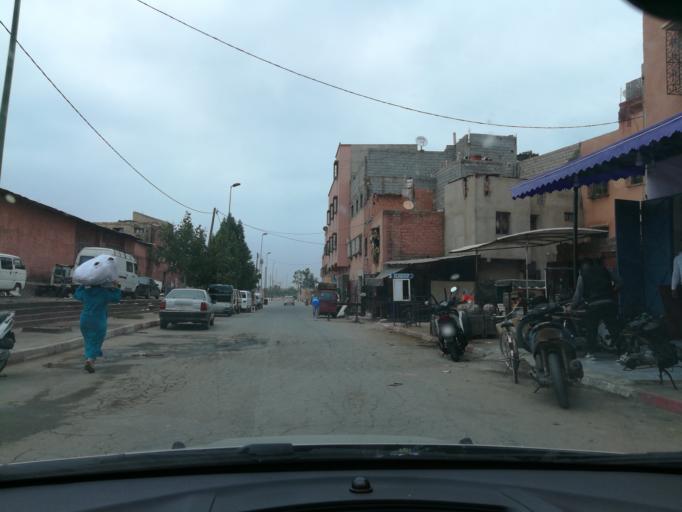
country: MA
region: Marrakech-Tensift-Al Haouz
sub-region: Marrakech
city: Marrakesh
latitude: 31.6472
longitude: -7.9855
